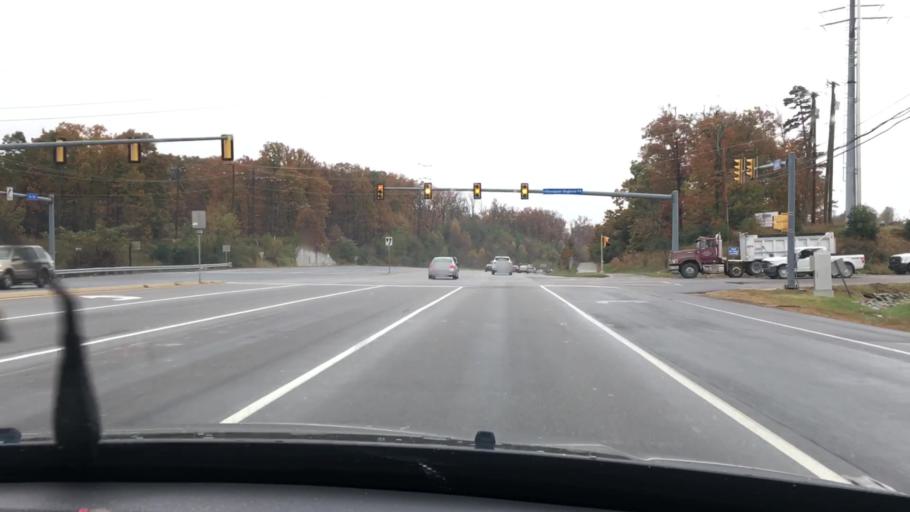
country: US
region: Virginia
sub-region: Fairfax County
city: Lorton
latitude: 38.6940
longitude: -77.2564
